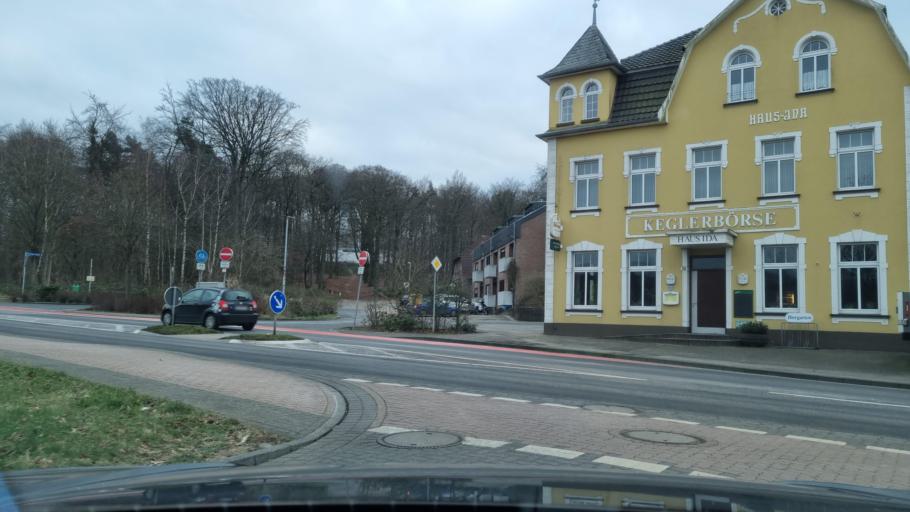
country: DE
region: North Rhine-Westphalia
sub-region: Regierungsbezirk Dusseldorf
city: Kleve
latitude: 51.7905
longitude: 6.1134
